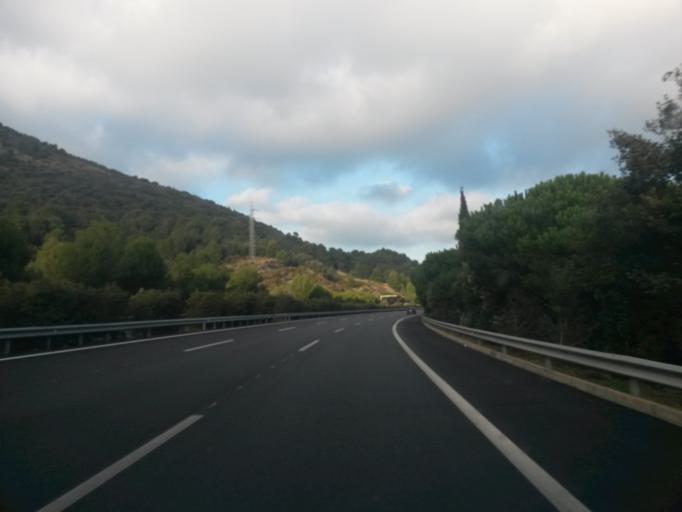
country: ES
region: Catalonia
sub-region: Provincia de Barcelona
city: Pineda de Mar
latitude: 41.6369
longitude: 2.6722
